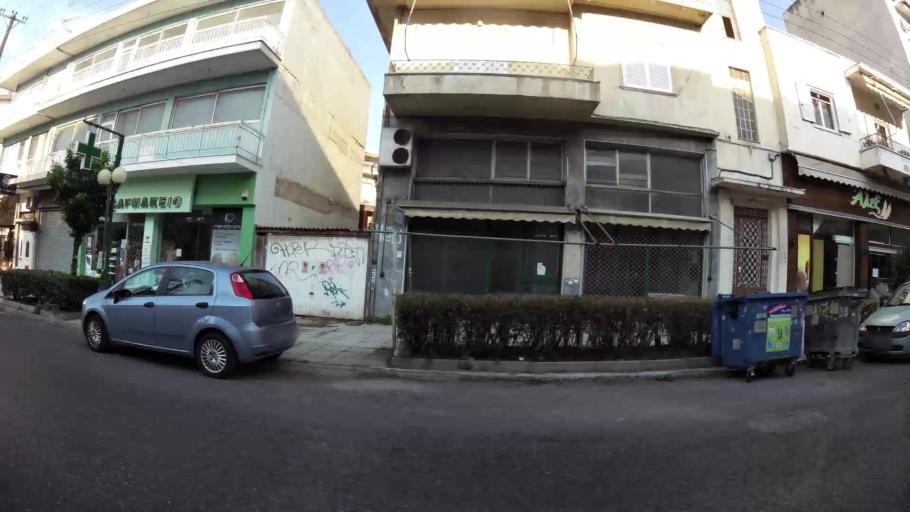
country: GR
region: Attica
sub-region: Nomarchia Athinas
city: Nea Ionia
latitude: 38.0477
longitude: 23.7504
